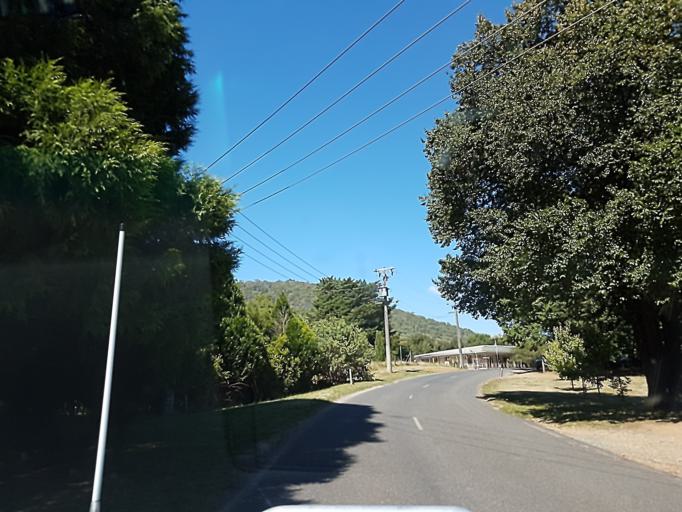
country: AU
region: Victoria
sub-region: Alpine
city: Mount Beauty
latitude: -36.7780
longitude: 146.9834
